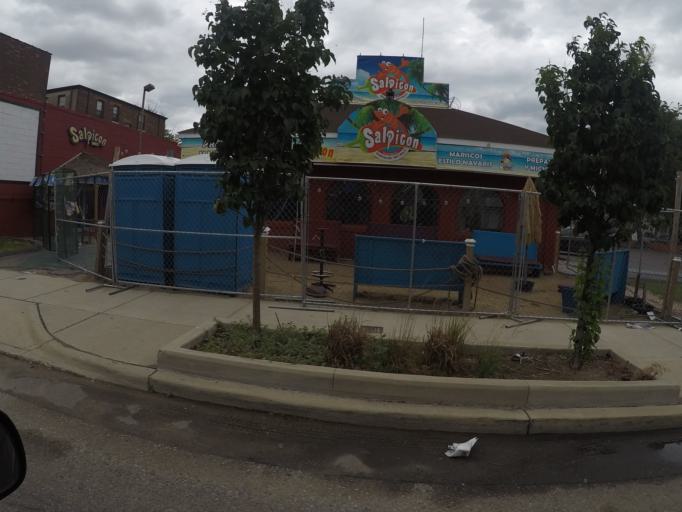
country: US
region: Michigan
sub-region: Wayne County
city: River Rouge
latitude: 42.3095
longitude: -83.1322
